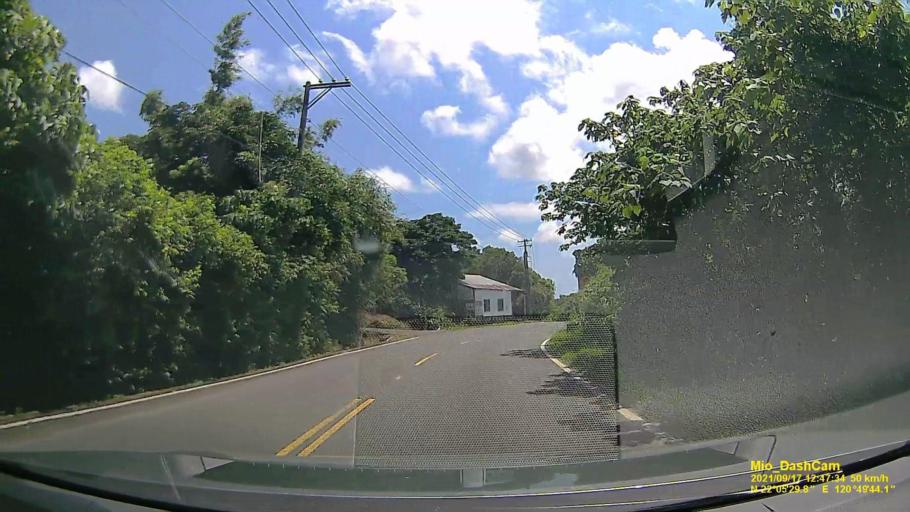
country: TW
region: Taiwan
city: Hengchun
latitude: 22.0915
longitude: 120.8289
